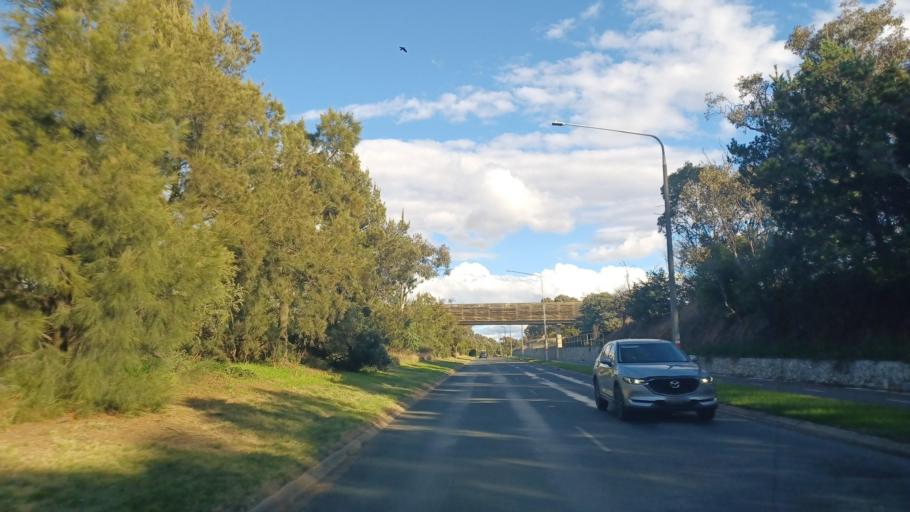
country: AU
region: Australian Capital Territory
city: Belconnen
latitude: -35.1878
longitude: 149.0720
